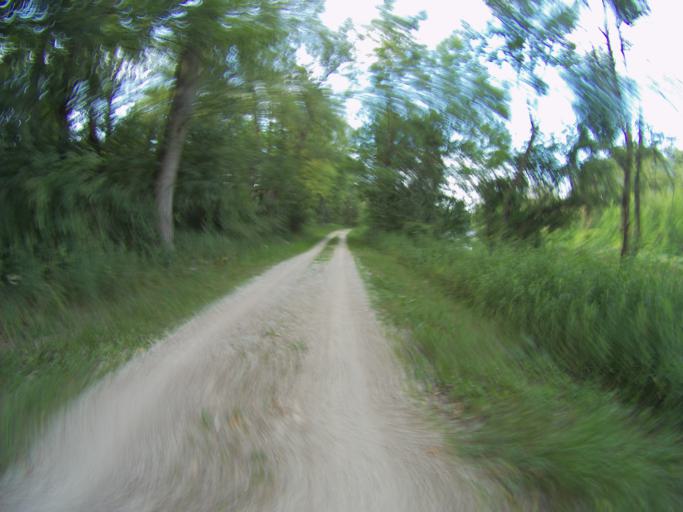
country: DE
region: Bavaria
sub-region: Upper Bavaria
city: Hallbergmoos
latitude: 48.3632
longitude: 11.7240
